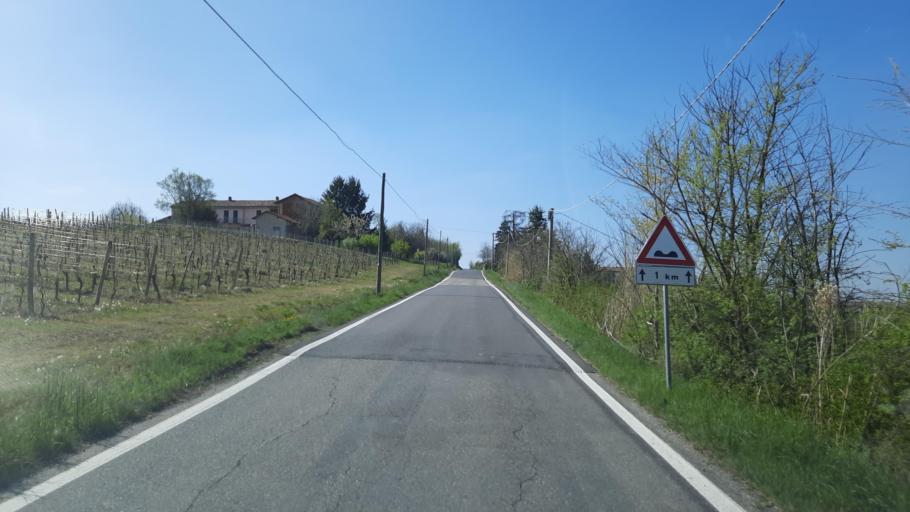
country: IT
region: Piedmont
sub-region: Provincia di Alessandria
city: Olivola
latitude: 45.0149
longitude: 8.3674
